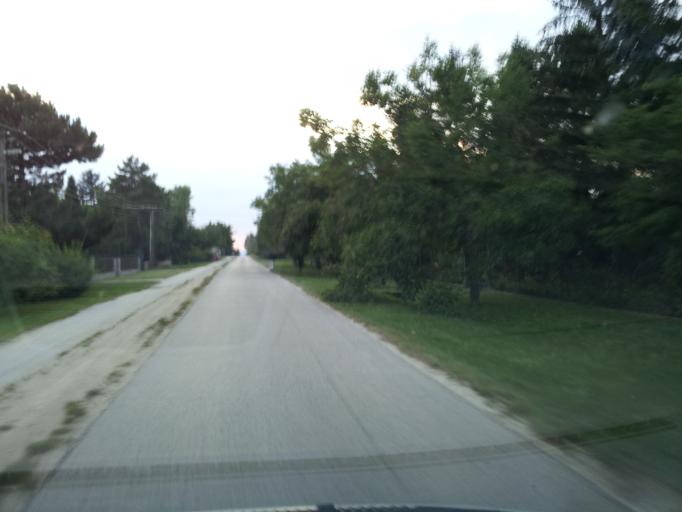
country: HU
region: Veszprem
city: Balatonkenese
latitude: 47.0228
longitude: 18.1525
